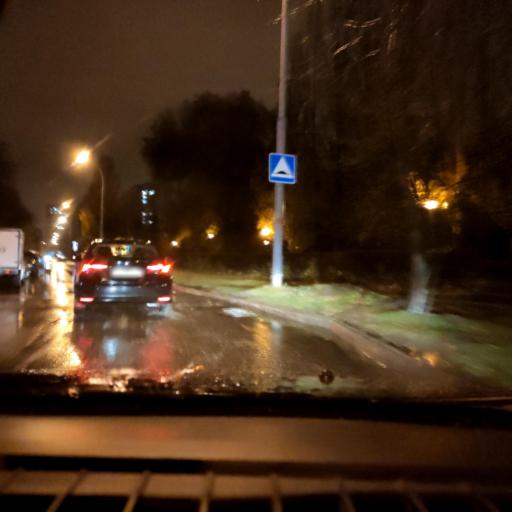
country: RU
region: Samara
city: Tol'yatti
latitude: 53.5314
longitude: 49.3047
